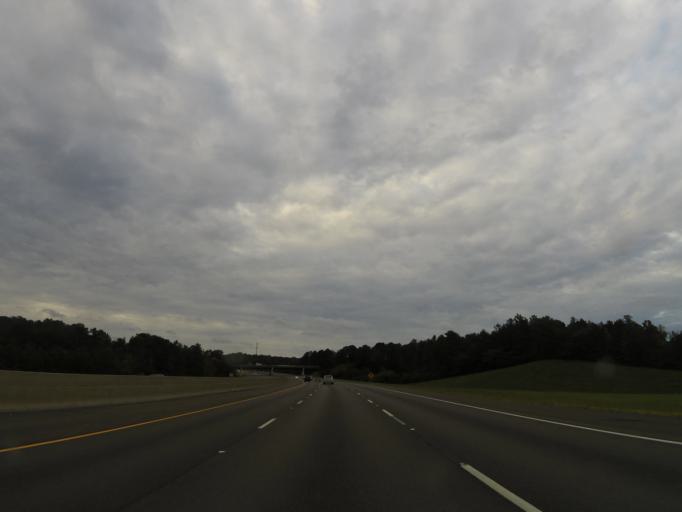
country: US
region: Alabama
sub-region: Jefferson County
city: Trussville
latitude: 33.5726
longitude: -86.6380
